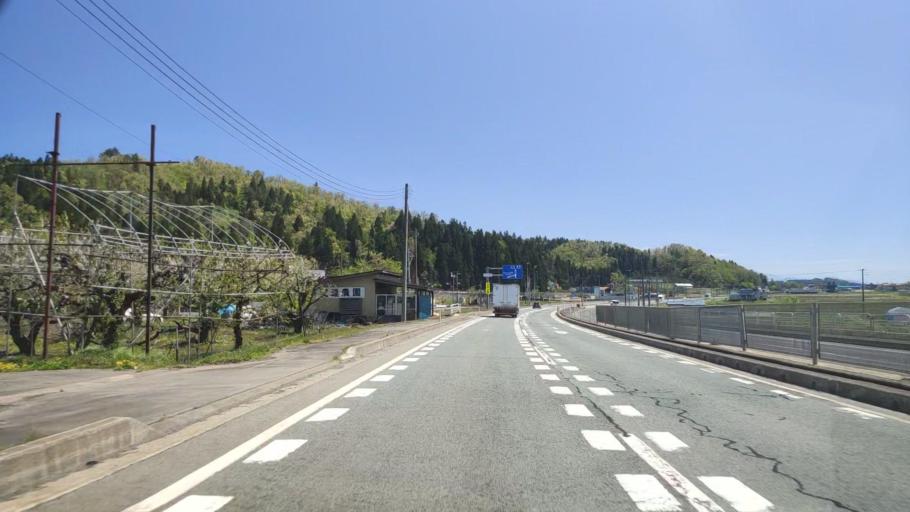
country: JP
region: Yamagata
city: Obanazawa
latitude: 38.5276
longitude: 140.3948
